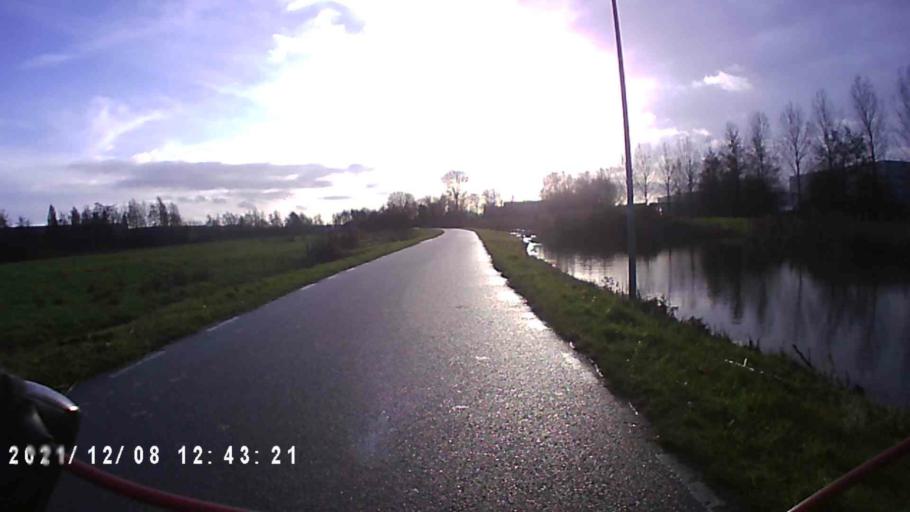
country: NL
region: Groningen
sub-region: Gemeente Groningen
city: Oosterpark
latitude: 53.2103
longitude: 6.6178
